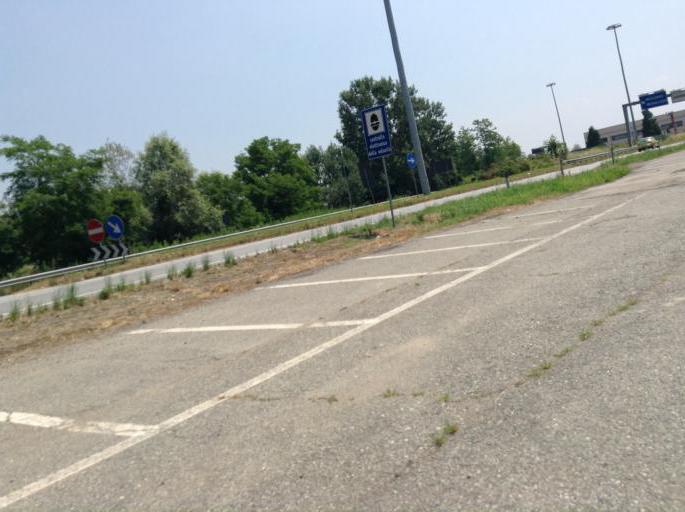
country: IT
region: Piedmont
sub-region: Provincia di Torino
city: Carignano
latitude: 44.9181
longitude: 7.6748
